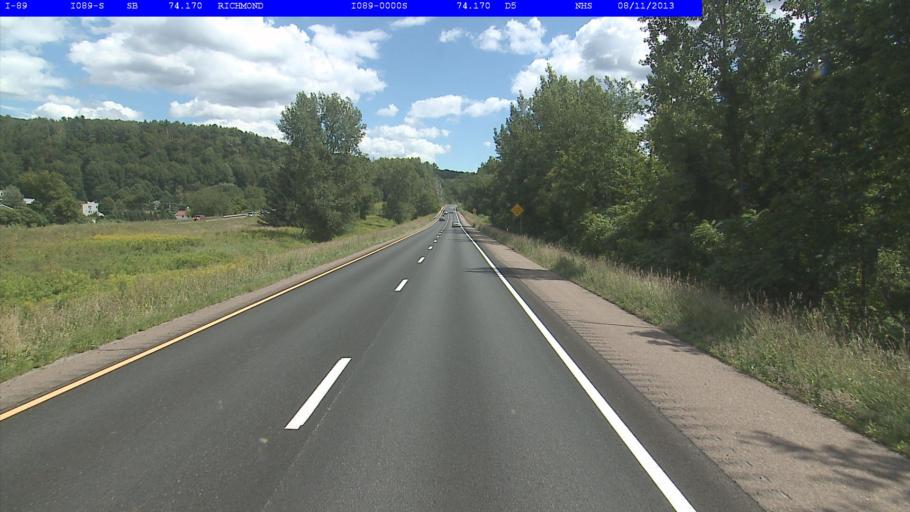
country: US
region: Vermont
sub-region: Chittenden County
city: Jericho
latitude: 44.3888
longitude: -72.9467
